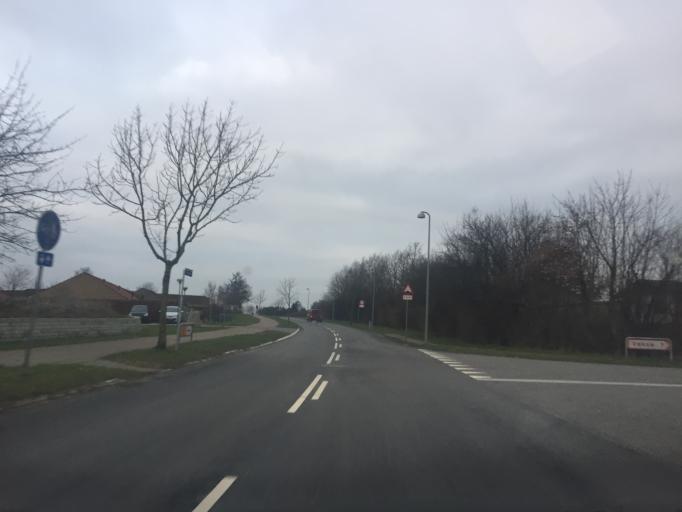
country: DK
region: Zealand
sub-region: Roskilde Kommune
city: Gundsomagle
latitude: 55.7369
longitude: 12.1594
